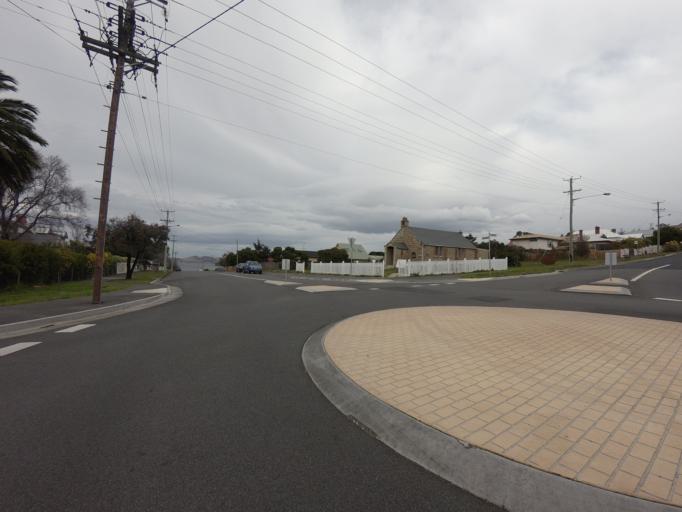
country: AU
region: Tasmania
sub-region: Clarence
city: Bellerive
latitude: -42.8770
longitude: 147.3692
